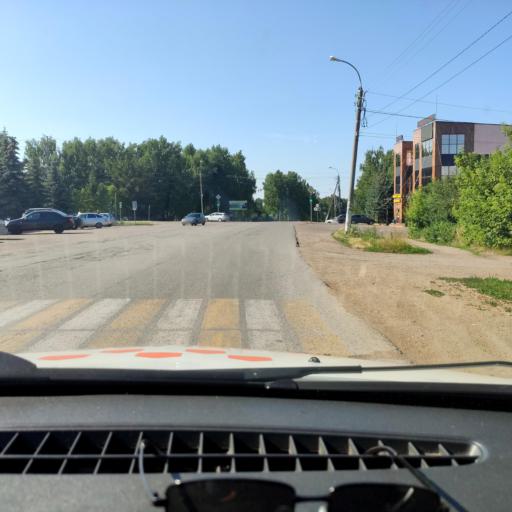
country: RU
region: Bashkortostan
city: Tolbazy
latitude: 54.0103
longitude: 55.8874
